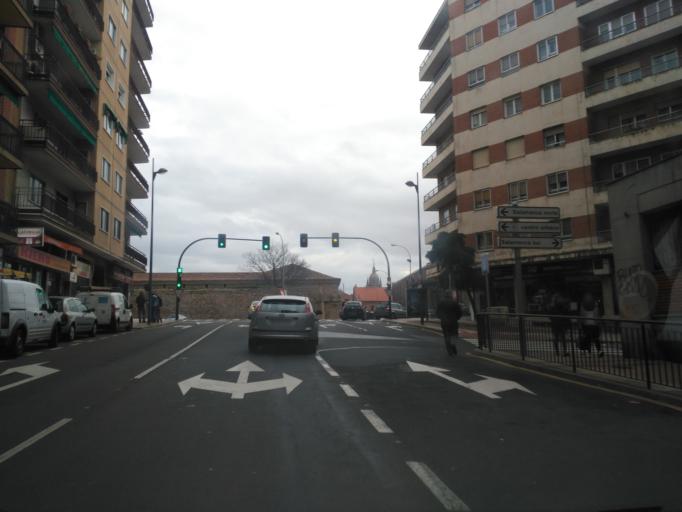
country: ES
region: Castille and Leon
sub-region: Provincia de Salamanca
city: Salamanca
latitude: 40.9662
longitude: -5.6716
